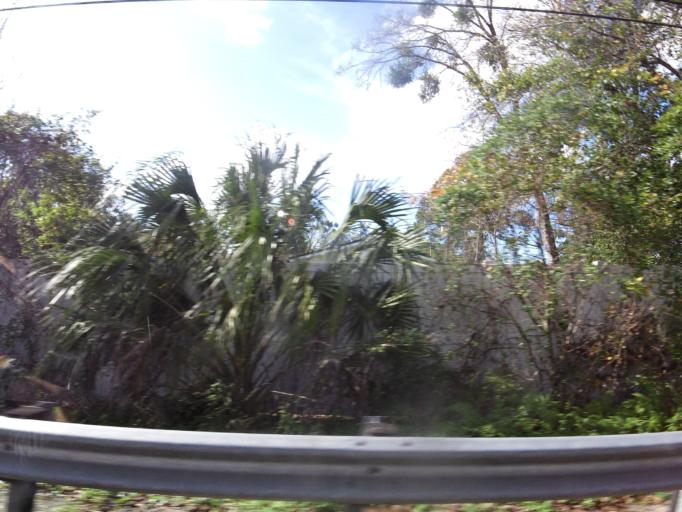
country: US
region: Florida
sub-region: Duval County
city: Jacksonville
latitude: 30.3331
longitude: -81.5603
